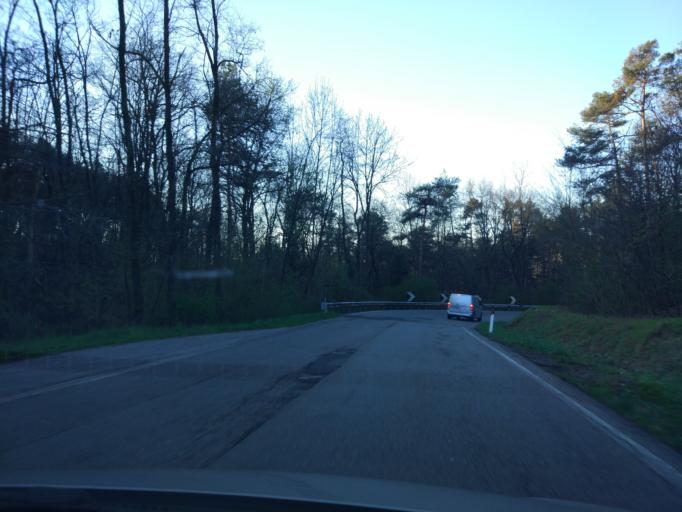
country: IT
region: Lombardy
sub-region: Provincia di Como
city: Alzate Brianza
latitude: 45.7607
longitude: 9.1650
